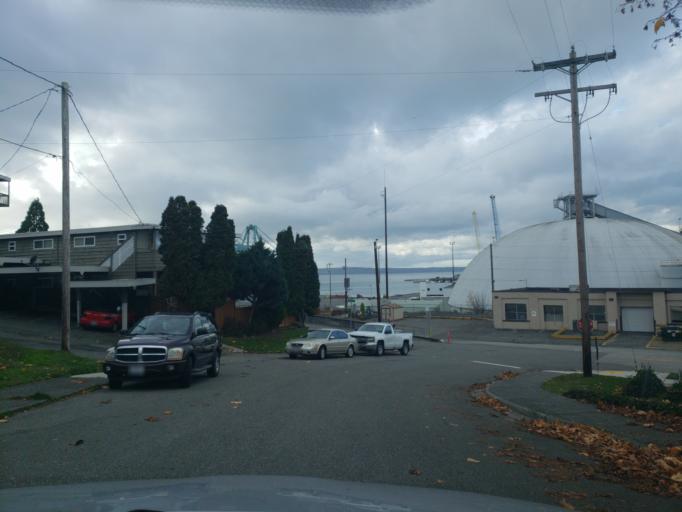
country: US
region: Washington
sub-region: Snohomish County
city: Everett
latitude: 47.9778
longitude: -122.2182
